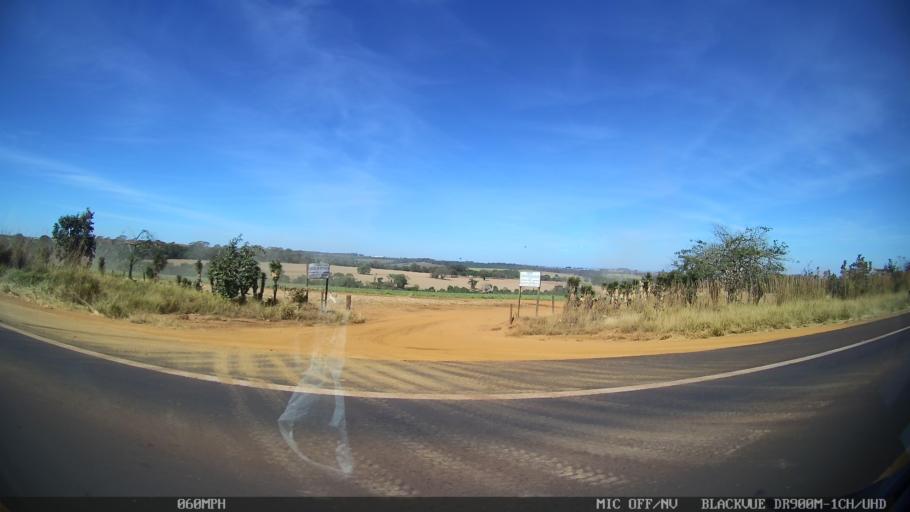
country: BR
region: Sao Paulo
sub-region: Franca
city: Franca
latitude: -20.5498
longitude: -47.4841
